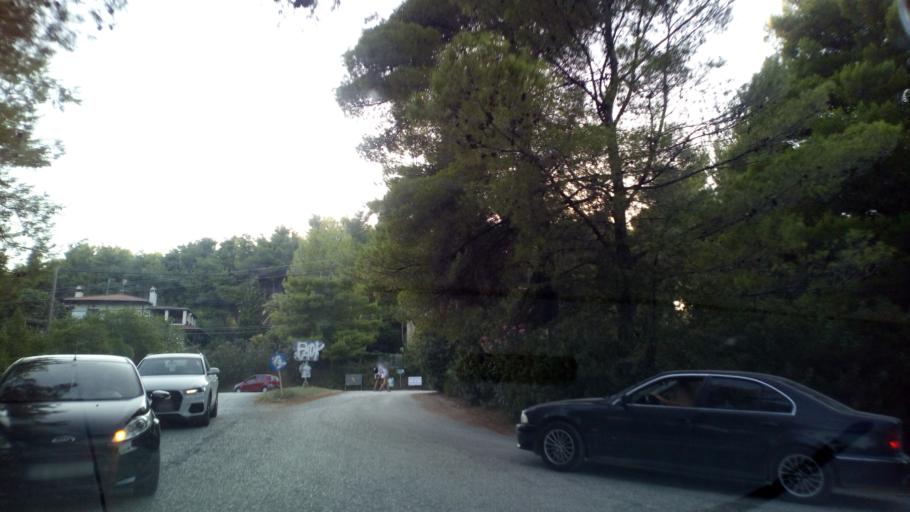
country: GR
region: Central Macedonia
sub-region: Nomos Chalkidikis
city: Pefkochori
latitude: 39.9591
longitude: 23.6750
